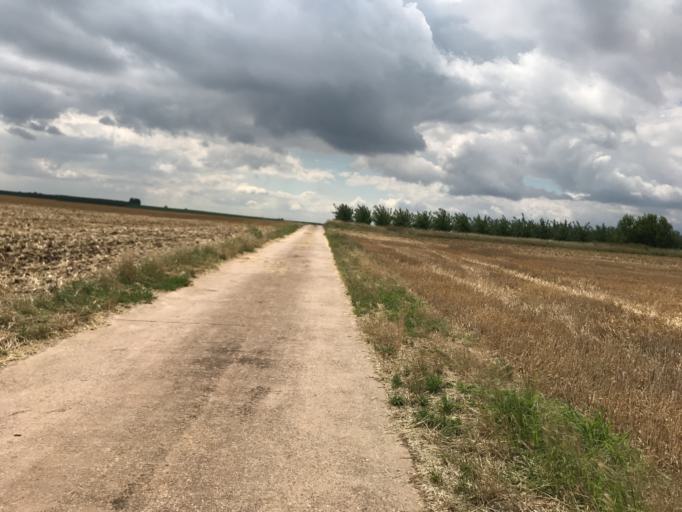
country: DE
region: Rheinland-Pfalz
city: Essenheim
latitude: 49.9502
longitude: 8.1506
